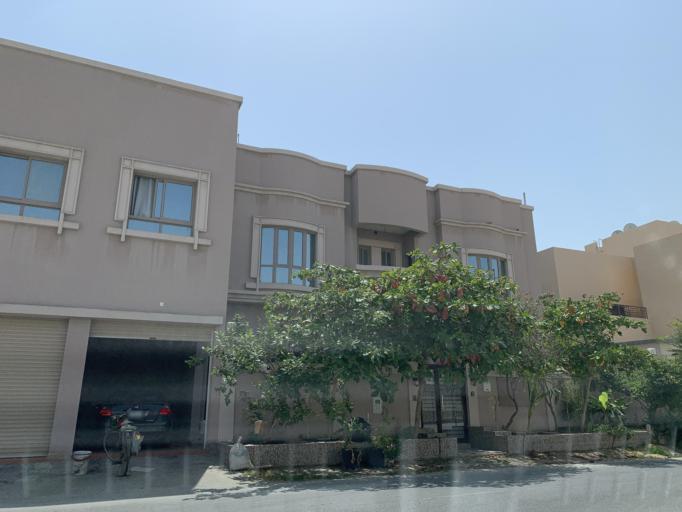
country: BH
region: Northern
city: Madinat `Isa
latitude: 26.1895
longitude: 50.5446
